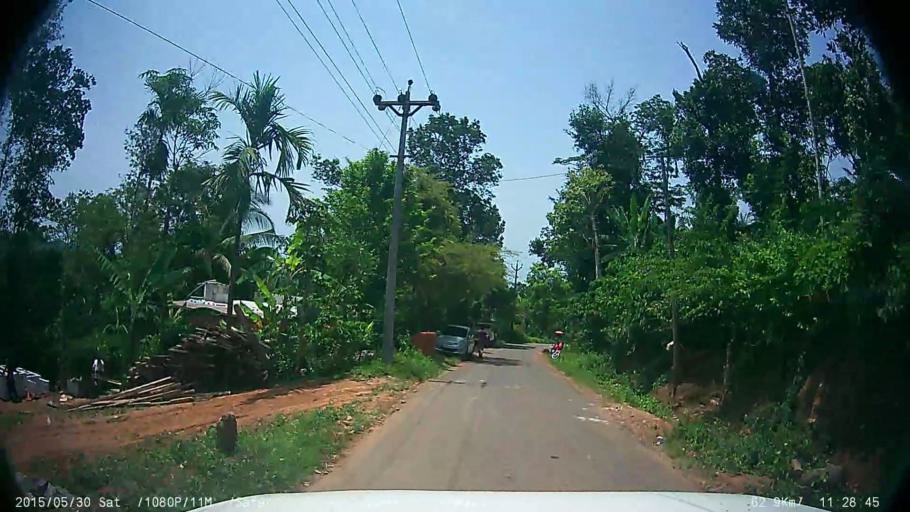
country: IN
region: Kerala
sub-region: Wayanad
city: Panamaram
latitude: 11.8117
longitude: 76.0465
